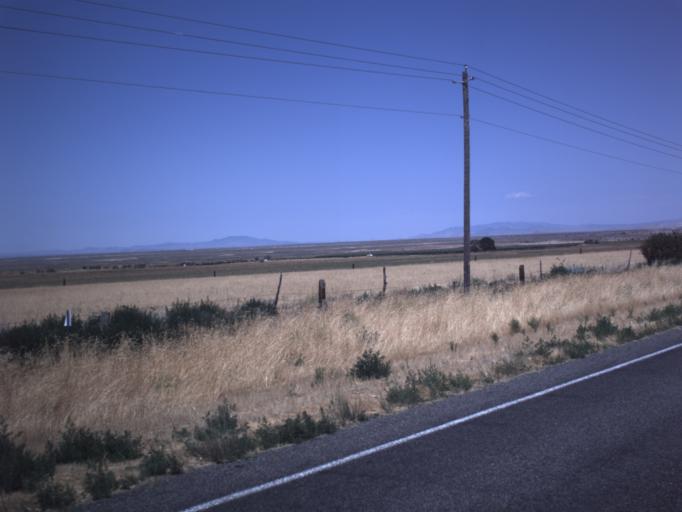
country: US
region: Utah
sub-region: Millard County
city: Delta
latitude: 39.3963
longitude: -112.3355
